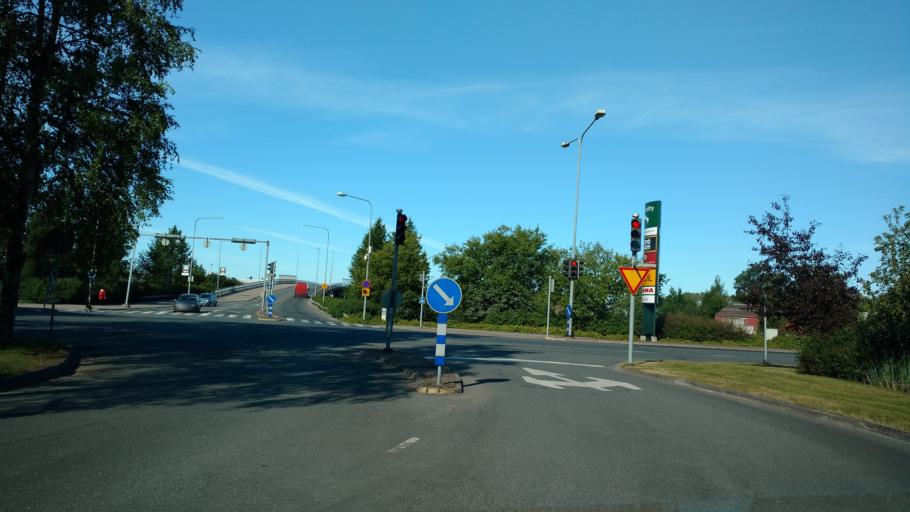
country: FI
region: Varsinais-Suomi
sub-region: Salo
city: Salo
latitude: 60.3892
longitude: 23.1184
